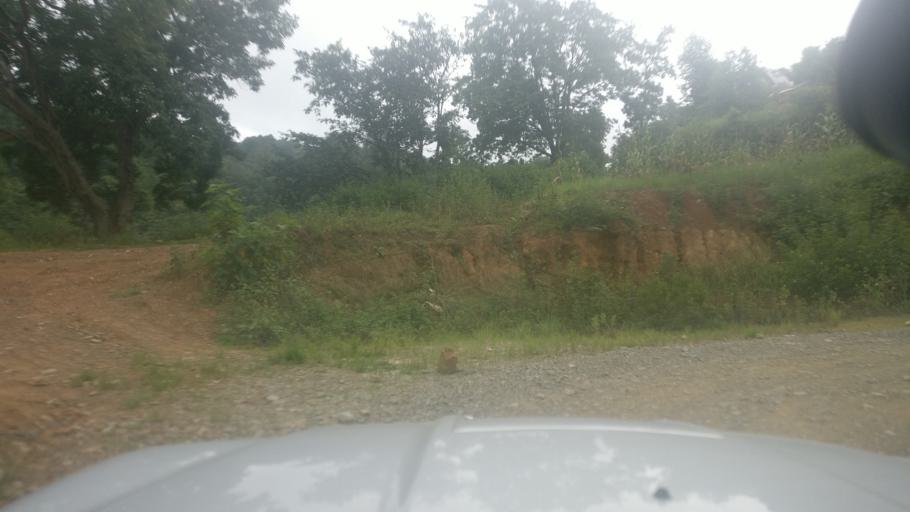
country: NP
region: Central Region
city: Kirtipur
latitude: 27.7046
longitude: 85.2536
